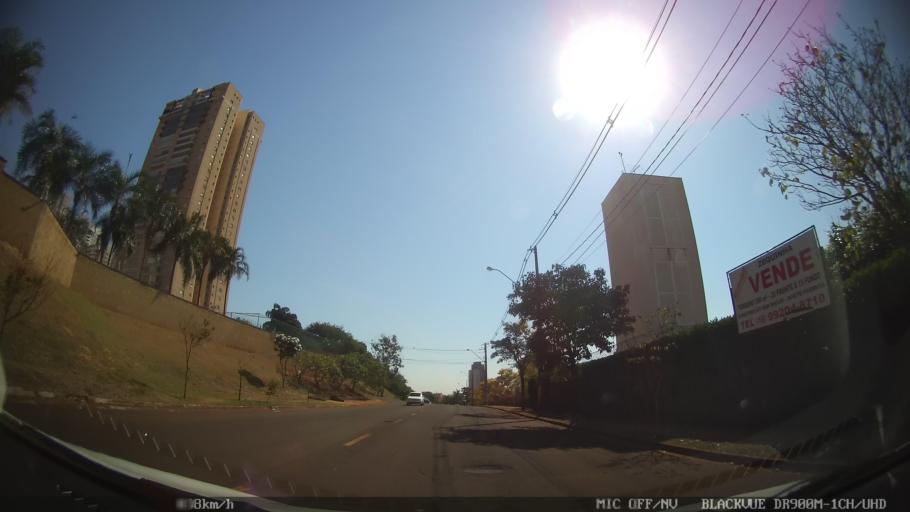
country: BR
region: Sao Paulo
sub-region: Ribeirao Preto
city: Ribeirao Preto
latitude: -21.2172
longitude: -47.8015
